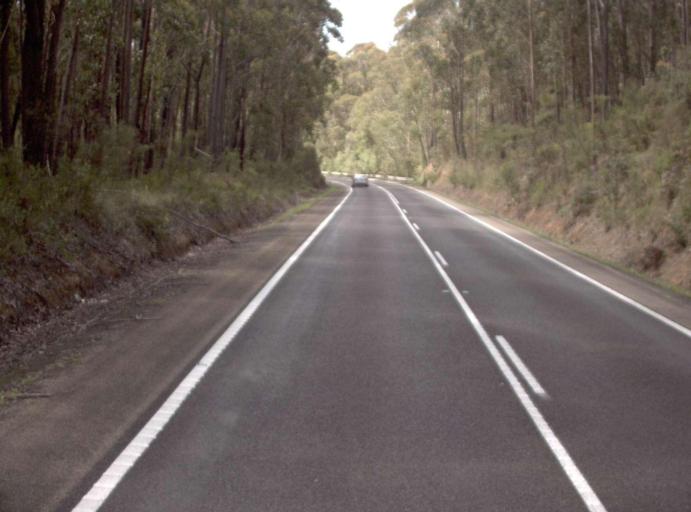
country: AU
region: New South Wales
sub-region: Bombala
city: Bombala
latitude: -37.5438
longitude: 149.3671
